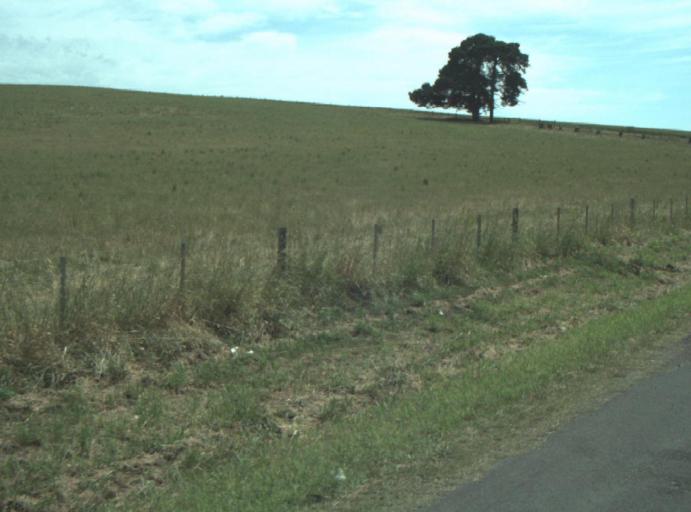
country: AU
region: Victoria
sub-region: Greater Geelong
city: Clifton Springs
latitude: -38.1473
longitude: 144.5960
